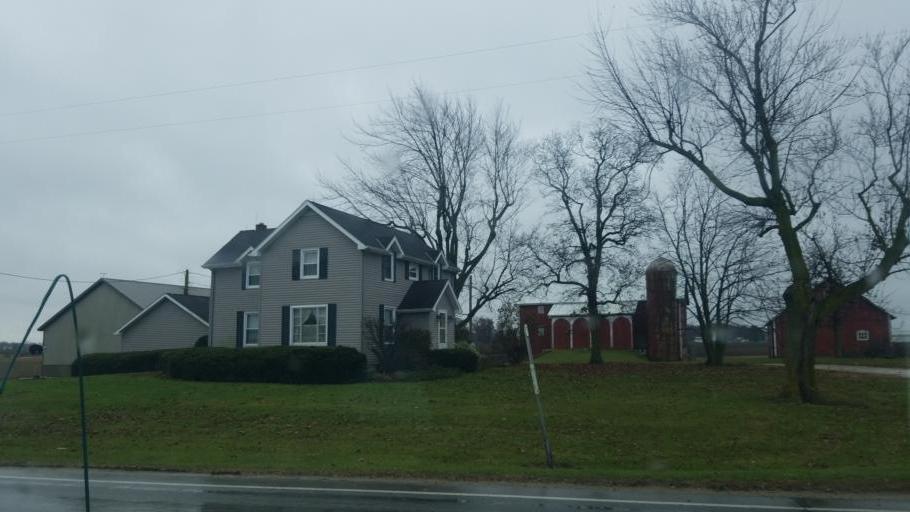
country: US
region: Indiana
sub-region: Adams County
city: Berne
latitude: 40.6584
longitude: -84.9179
